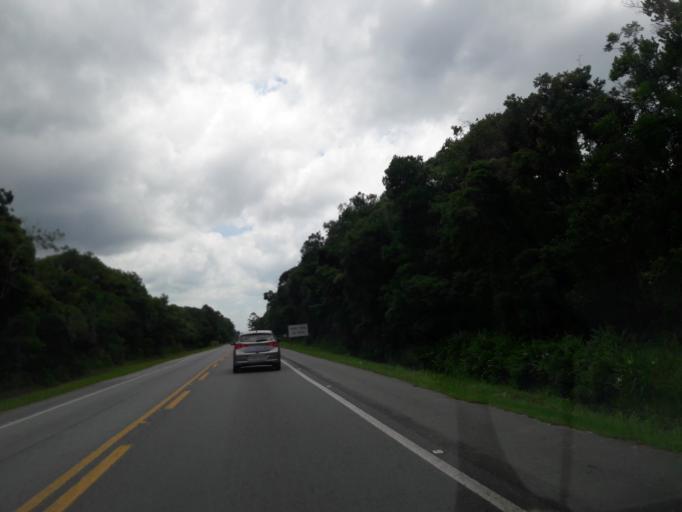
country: BR
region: Parana
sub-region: Pontal Do Parana
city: Pontal do Parana
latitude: -25.6685
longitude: -48.5163
